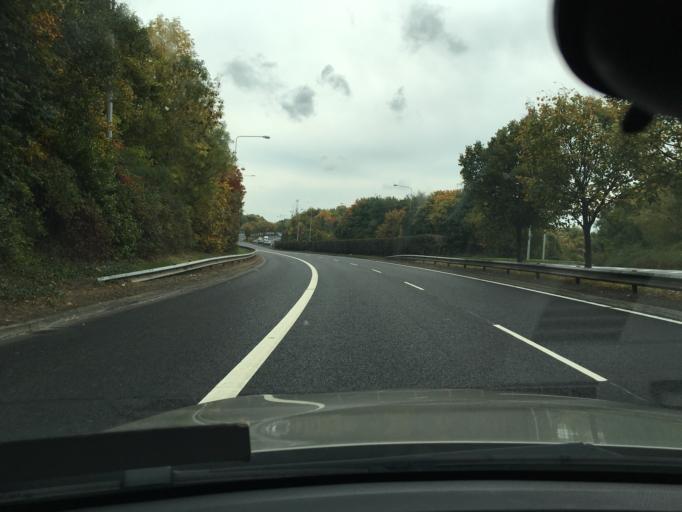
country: IE
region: Leinster
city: Ballyfermot
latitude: 53.3506
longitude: -6.3558
